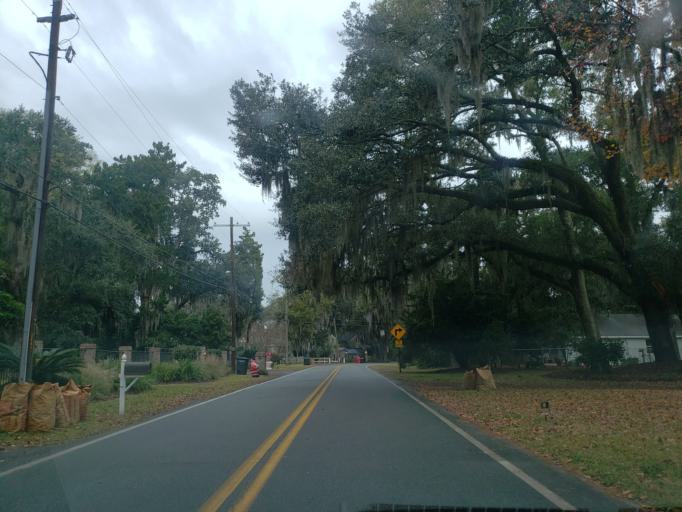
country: US
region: Georgia
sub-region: Chatham County
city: Wilmington Island
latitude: 31.9743
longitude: -81.0005
